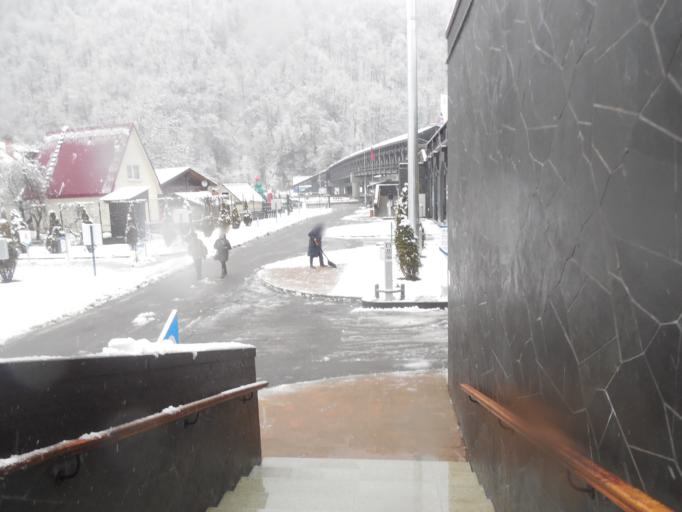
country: RU
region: Krasnodarskiy
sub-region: Sochi City
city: Krasnaya Polyana
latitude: 43.6765
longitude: 40.2825
